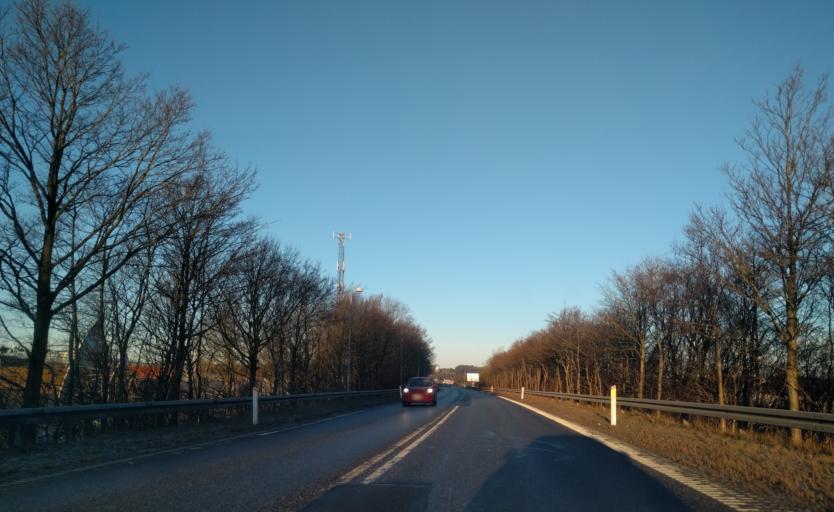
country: DK
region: North Denmark
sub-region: Alborg Kommune
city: Vestbjerg
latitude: 57.0868
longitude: 9.9641
